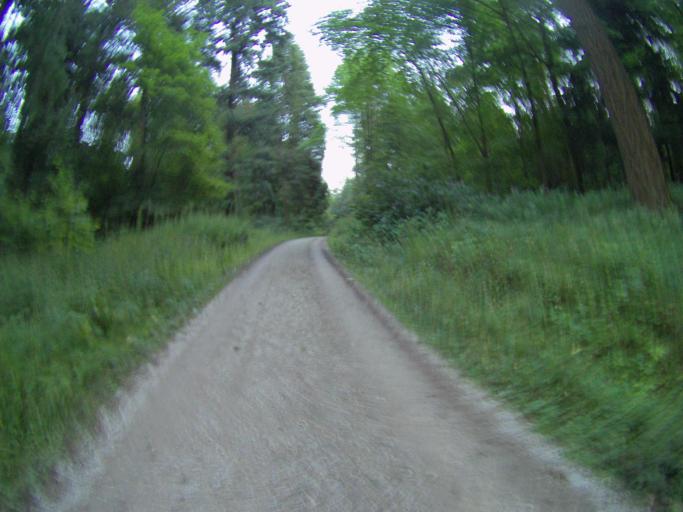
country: DE
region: Bavaria
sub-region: Upper Bavaria
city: Freising
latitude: 48.4215
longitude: 11.7255
